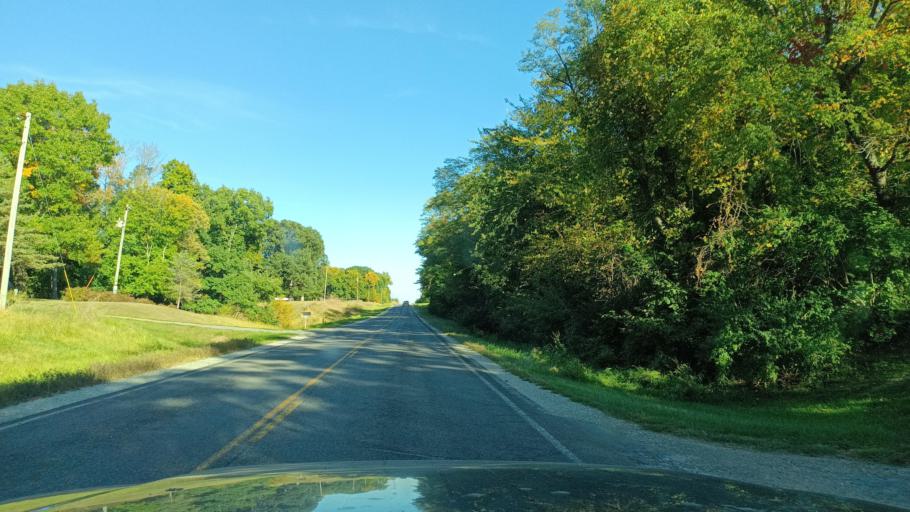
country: US
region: Illinois
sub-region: McLean County
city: Le Roy
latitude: 40.2244
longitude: -88.8146
